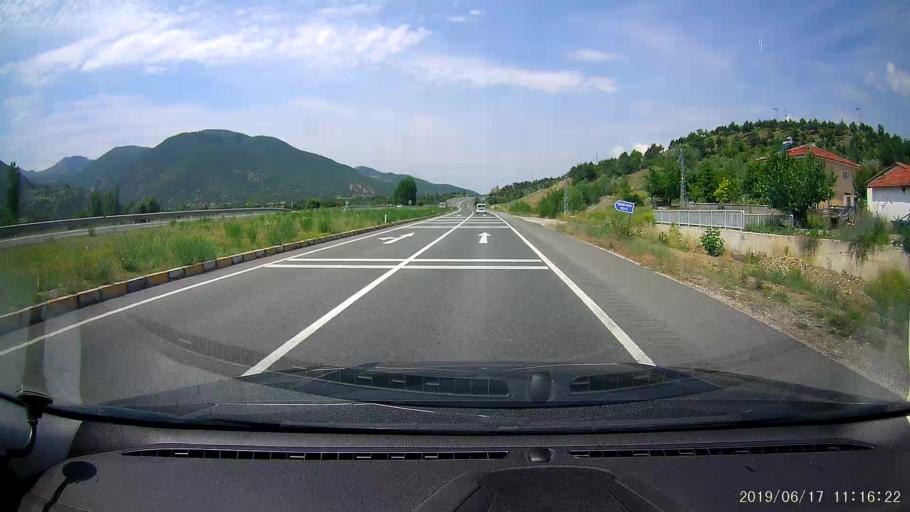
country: TR
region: Kastamonu
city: Tosya
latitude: 40.9464
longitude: 33.9012
